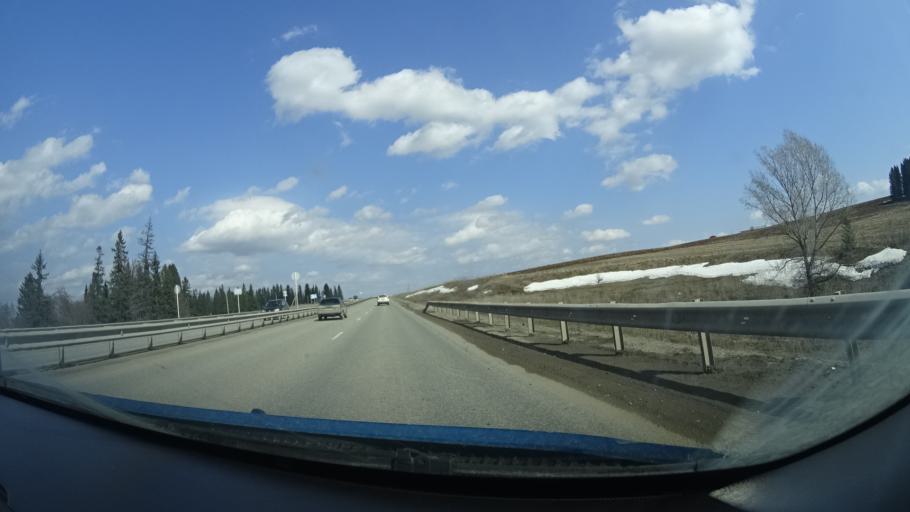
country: RU
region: Perm
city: Kultayevo
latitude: 57.8637
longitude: 55.8784
